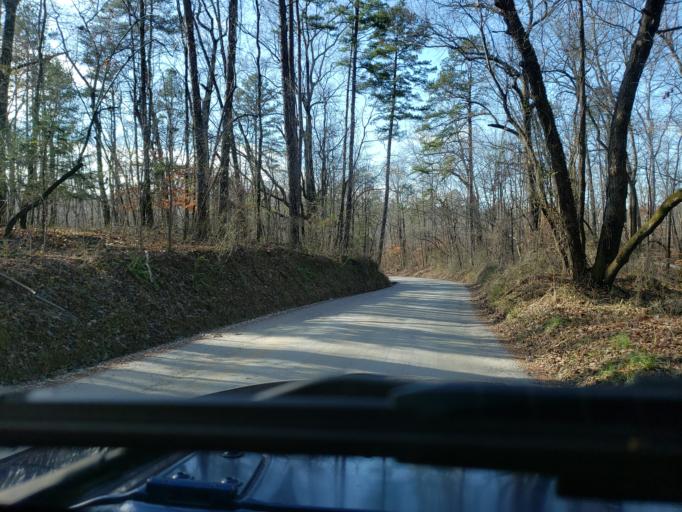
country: US
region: North Carolina
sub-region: Cleveland County
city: Kings Mountain
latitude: 35.1571
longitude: -81.3353
